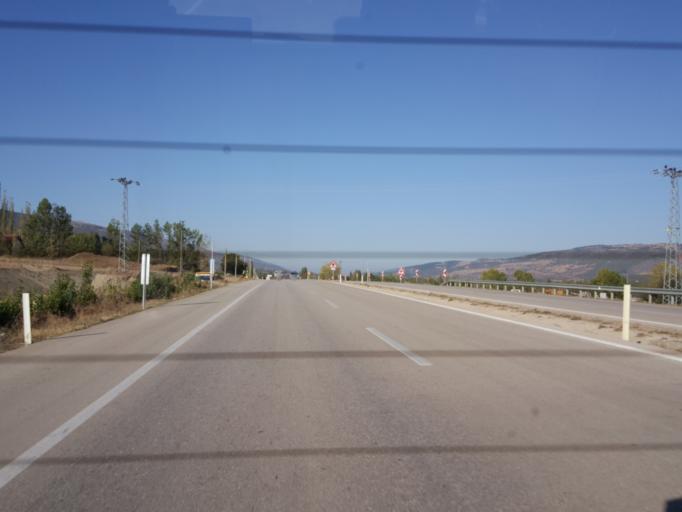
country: TR
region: Amasya
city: Ezinepazari
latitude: 40.5690
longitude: 36.0793
